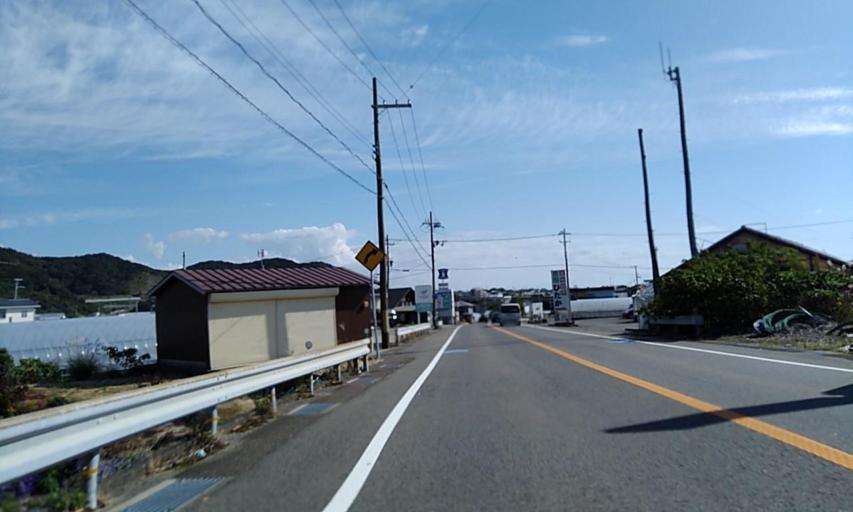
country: JP
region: Wakayama
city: Gobo
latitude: 33.8323
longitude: 135.1814
